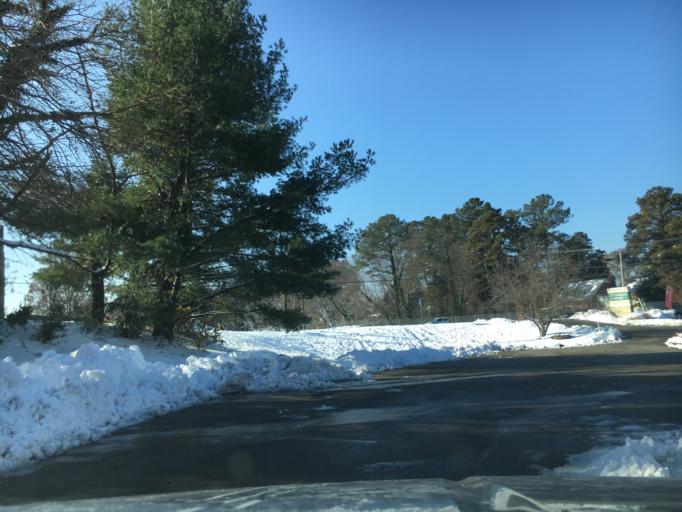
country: US
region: Virginia
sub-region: Henrico County
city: Tuckahoe
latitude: 37.5924
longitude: -77.5322
